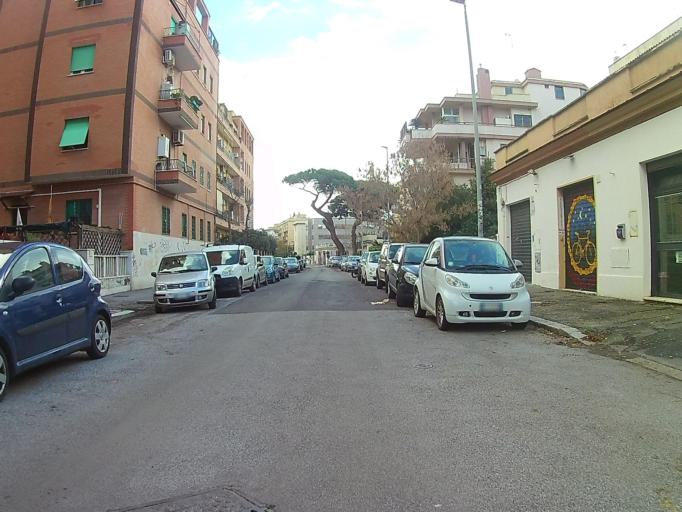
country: IT
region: Latium
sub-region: Citta metropolitana di Roma Capitale
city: Lido di Ostia
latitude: 41.7308
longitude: 12.2839
